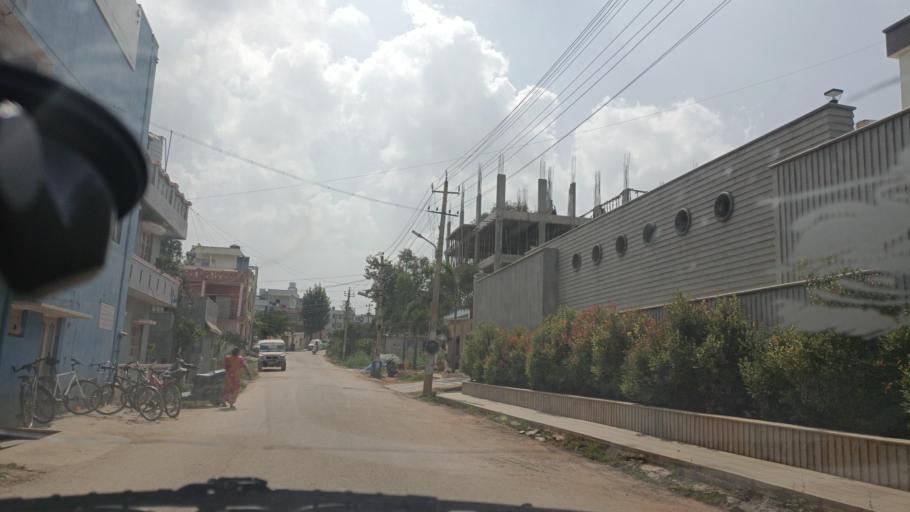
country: IN
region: Karnataka
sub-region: Bangalore Urban
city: Yelahanka
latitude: 13.1685
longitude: 77.6346
